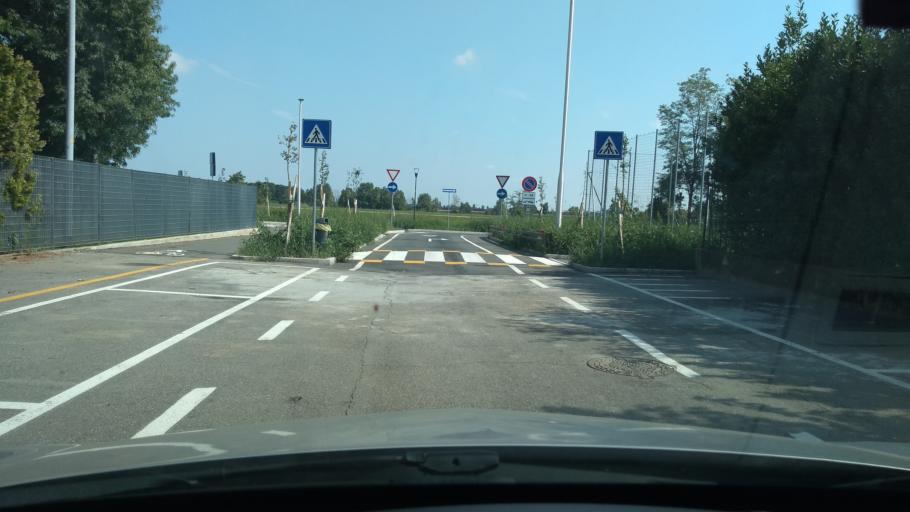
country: IT
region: Lombardy
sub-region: Provincia di Bergamo
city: Lallio
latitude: 45.6693
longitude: 9.6410
